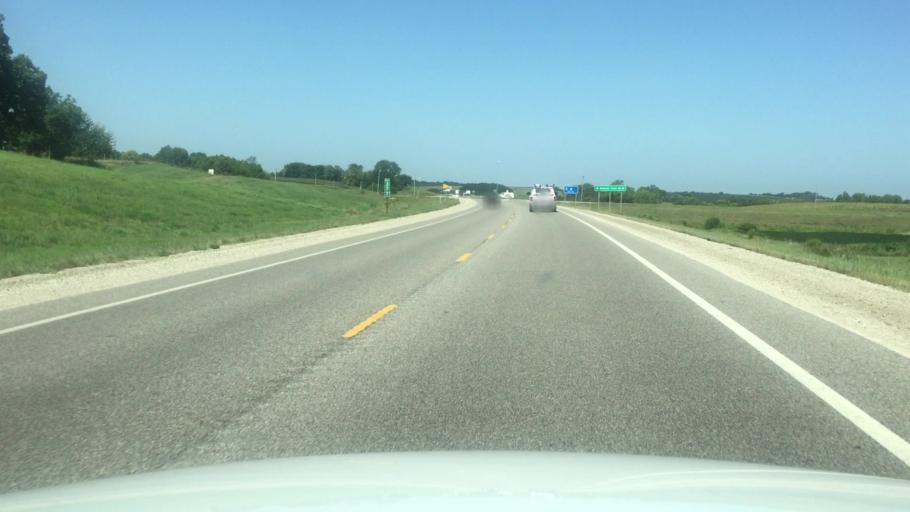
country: US
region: Kansas
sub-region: Doniphan County
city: Troy
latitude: 39.7944
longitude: -95.0839
